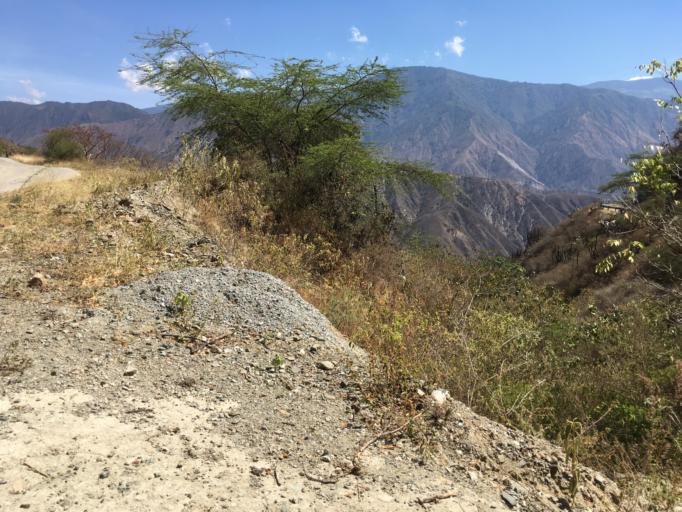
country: CO
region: Santander
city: Aratoca
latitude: 6.7778
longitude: -72.9955
